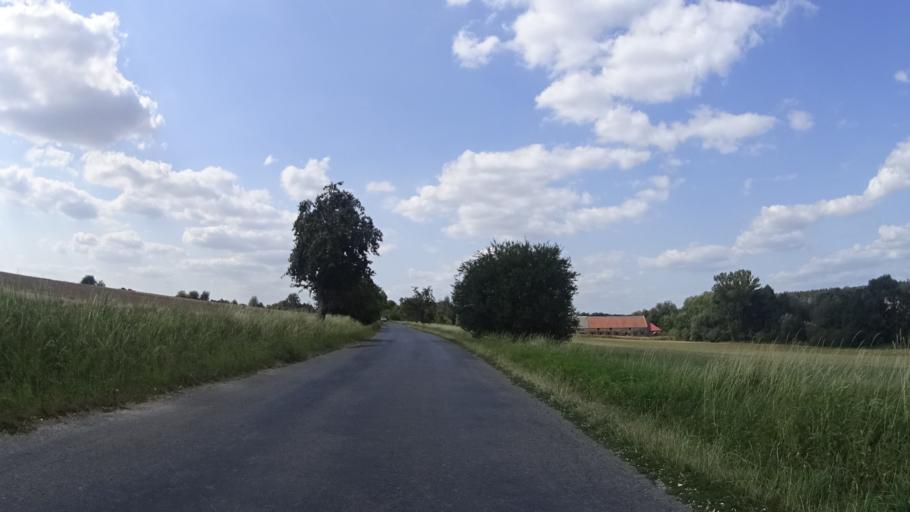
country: CZ
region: Kralovehradecky
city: Liban
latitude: 50.4005
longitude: 15.2789
